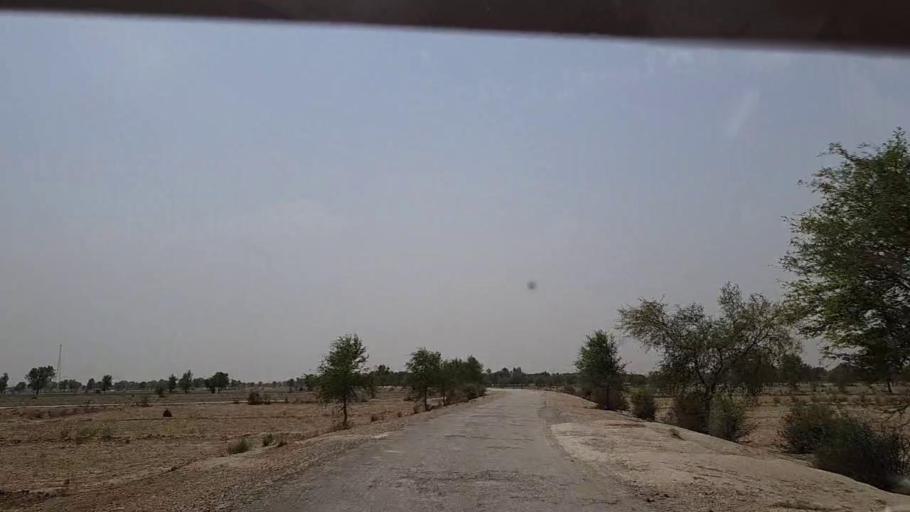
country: PK
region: Sindh
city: Khairpur Nathan Shah
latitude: 27.0165
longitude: 67.5984
